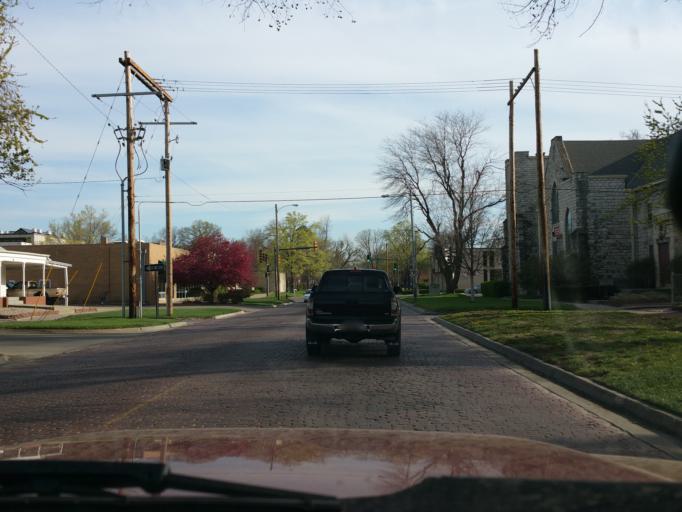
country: US
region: Kansas
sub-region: Riley County
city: Manhattan
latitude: 39.1804
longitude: -96.5668
